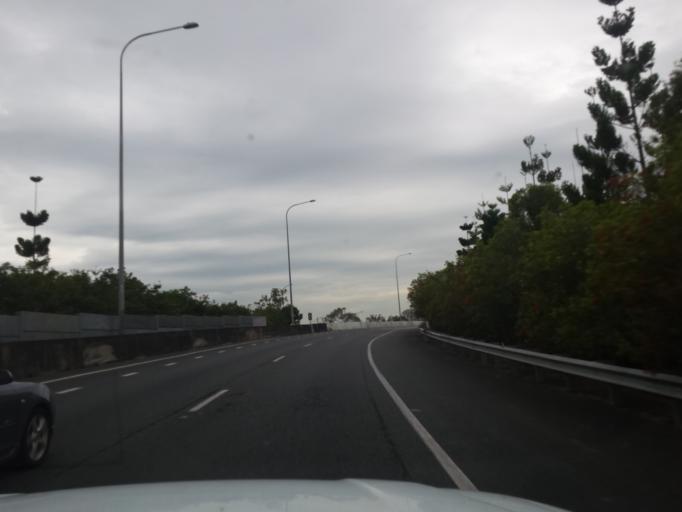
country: AU
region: Queensland
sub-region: Logan
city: Beenleigh
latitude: -27.6856
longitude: 153.1881
